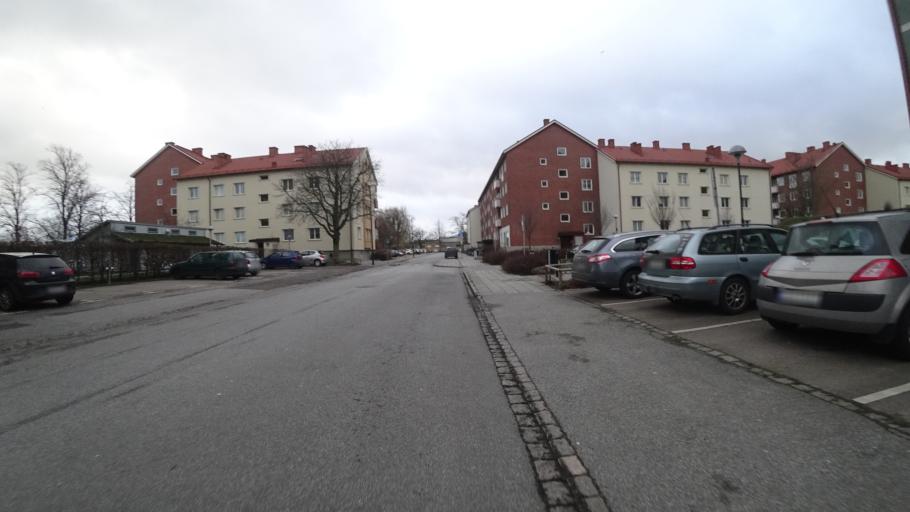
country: SE
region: Skane
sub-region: Malmo
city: Malmoe
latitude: 55.5793
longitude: 13.0272
